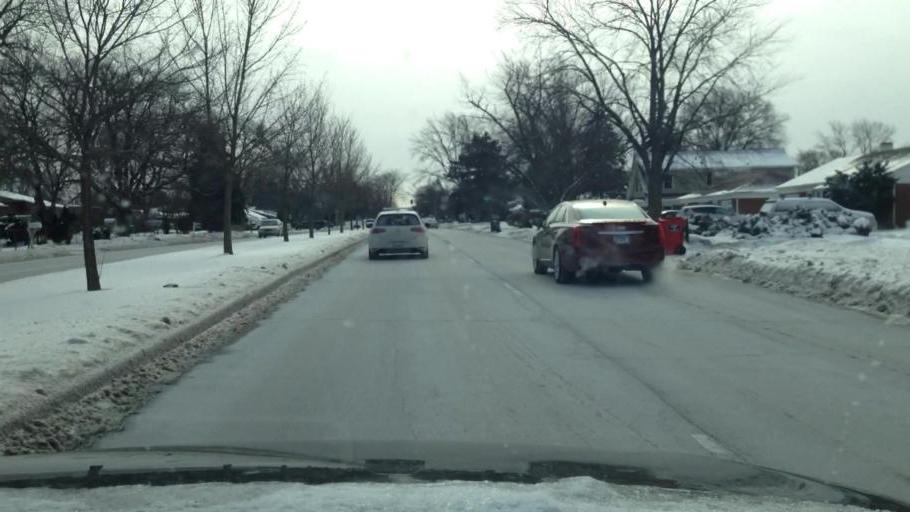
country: US
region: Illinois
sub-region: DuPage County
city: Lombard
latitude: 41.8563
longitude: -88.0122
